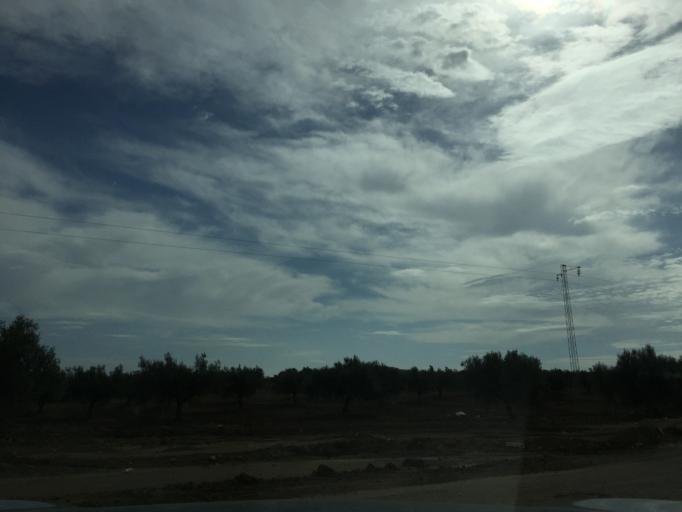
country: TN
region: Zaghwan
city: El Fahs
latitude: 36.2844
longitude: 9.8063
